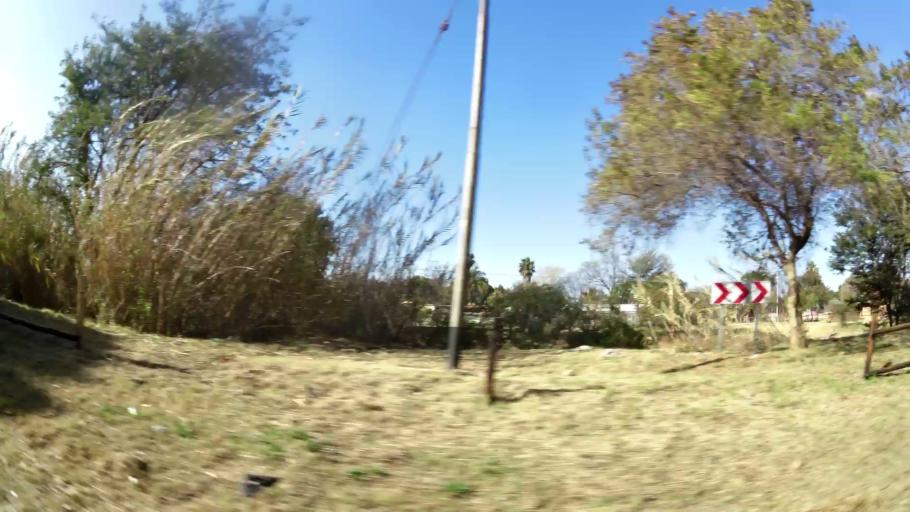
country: ZA
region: Gauteng
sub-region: City of Tshwane Metropolitan Municipality
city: Pretoria
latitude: -25.7239
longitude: 28.2629
